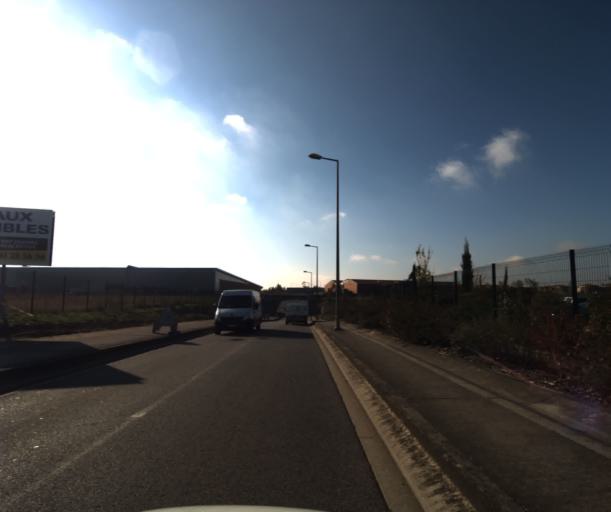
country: FR
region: Midi-Pyrenees
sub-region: Departement de la Haute-Garonne
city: Colomiers
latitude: 43.6033
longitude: 1.3603
